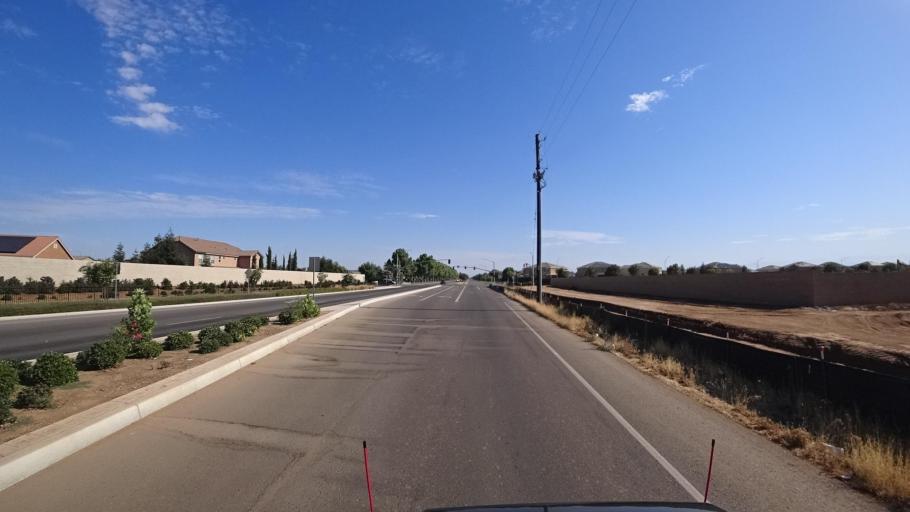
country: US
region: California
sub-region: Fresno County
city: Tarpey Village
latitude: 36.7783
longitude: -119.6640
